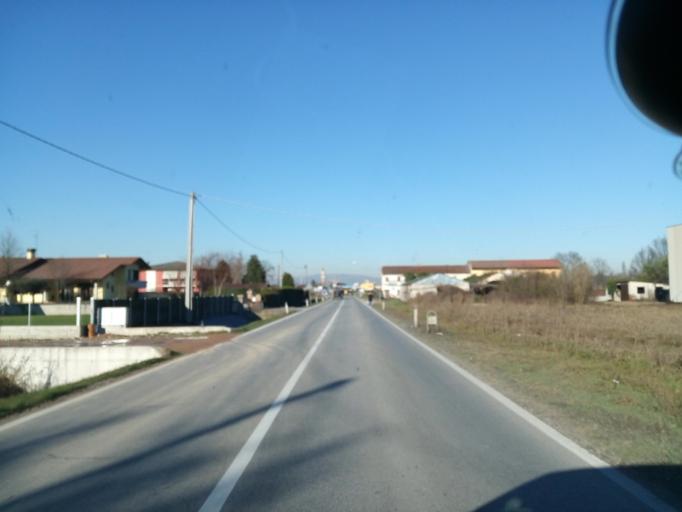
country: IT
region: Veneto
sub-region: Provincia di Padova
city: Massanzago-Ca' Baglioni-San Dono
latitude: 45.5684
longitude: 12.0034
